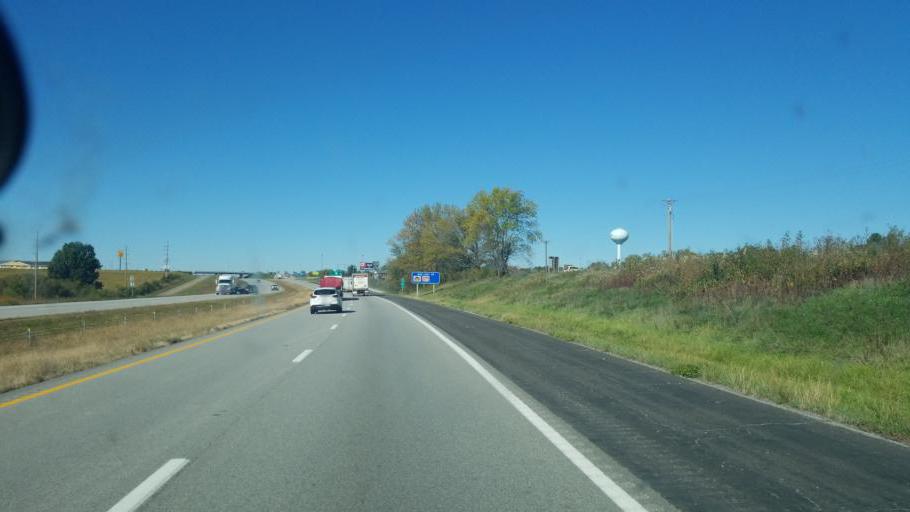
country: US
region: Missouri
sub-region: Lafayette County
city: Higginsville
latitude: 38.9998
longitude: -93.7270
